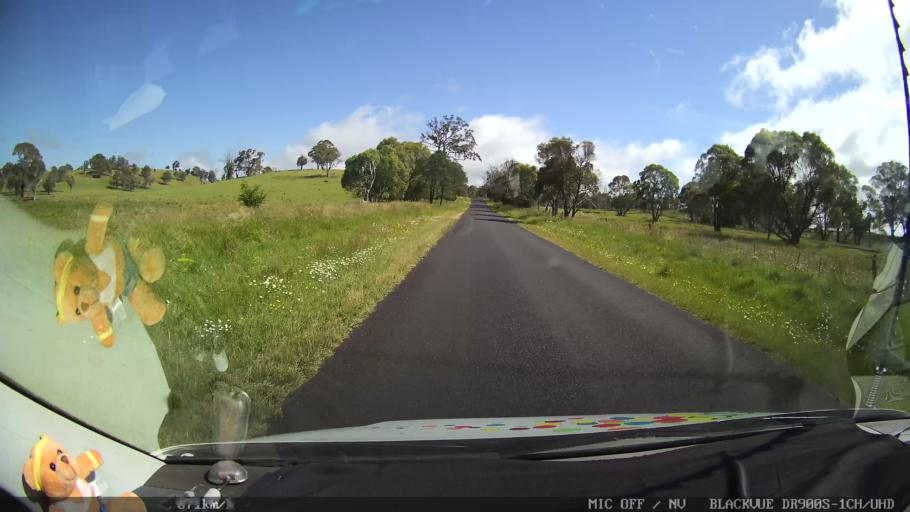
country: AU
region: New South Wales
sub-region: Guyra
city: Guyra
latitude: -30.0425
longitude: 151.6676
